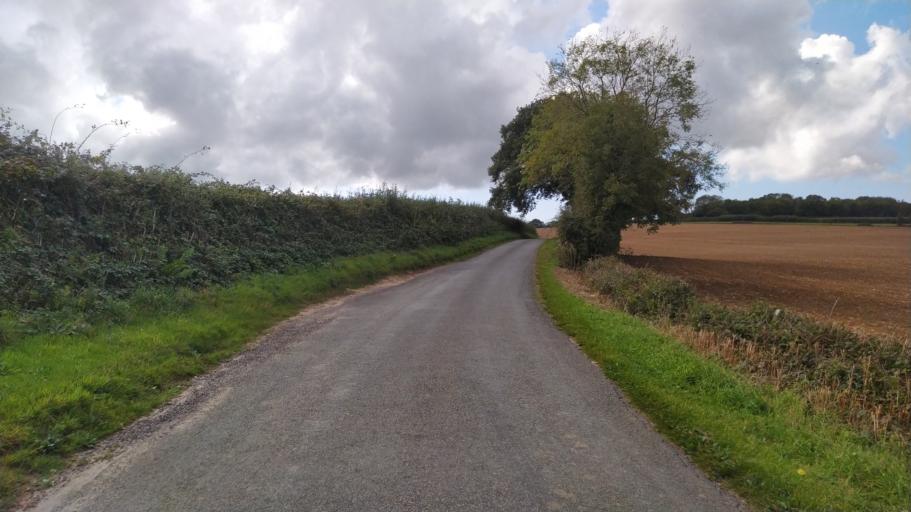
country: GB
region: England
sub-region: Dorset
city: Dorchester
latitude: 50.6776
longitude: -2.4162
